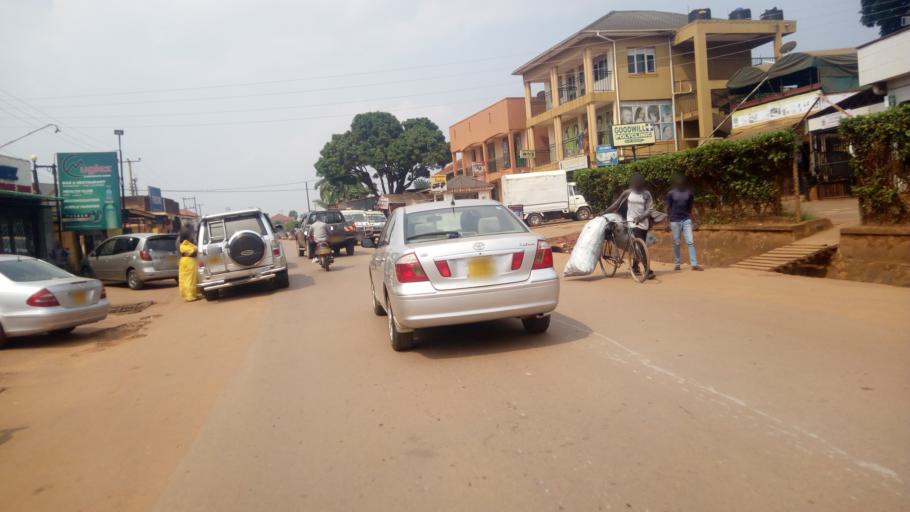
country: UG
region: Central Region
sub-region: Wakiso District
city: Kireka
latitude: 0.3213
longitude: 32.6374
